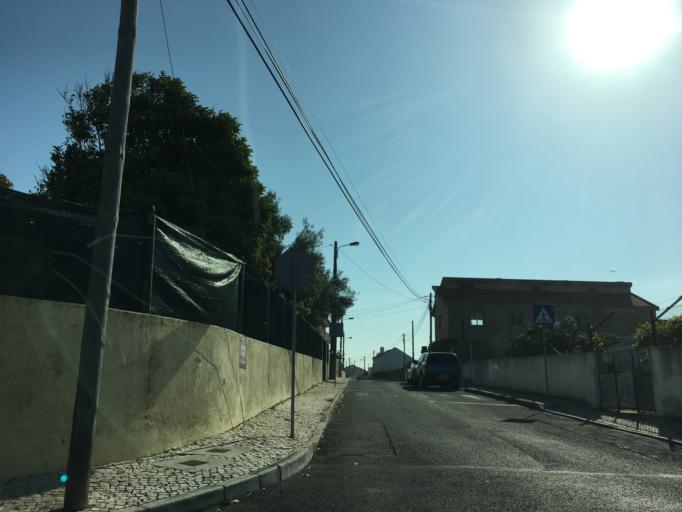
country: PT
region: Lisbon
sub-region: Cascais
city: Sao Domingos de Rana
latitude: 38.7194
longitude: -9.3427
